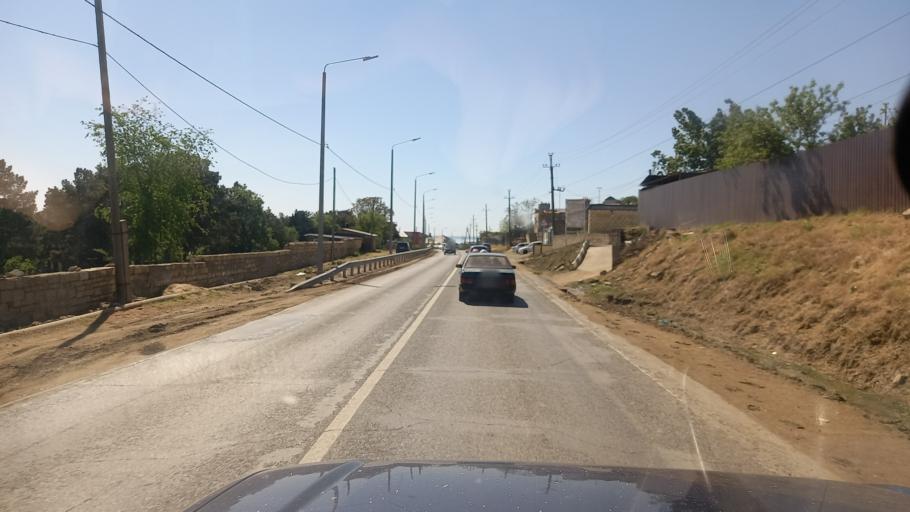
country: RU
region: Dagestan
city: Derbent
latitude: 42.0477
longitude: 48.2839
